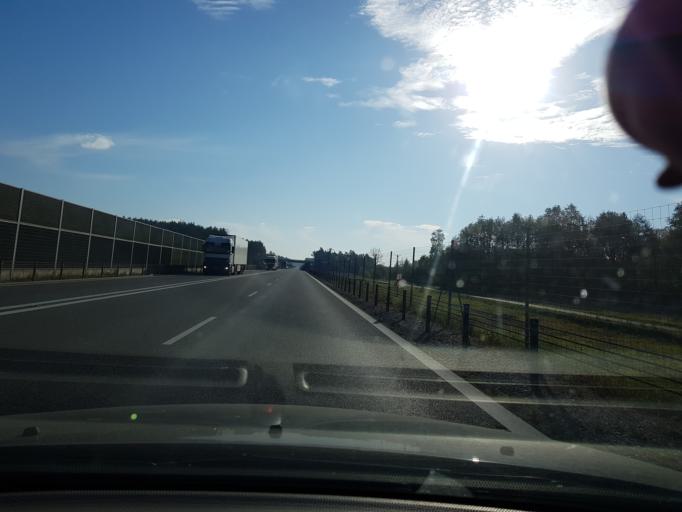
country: PL
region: Masovian Voivodeship
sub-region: Powiat zyrardowski
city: Zyrardow
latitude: 52.0226
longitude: 20.4535
